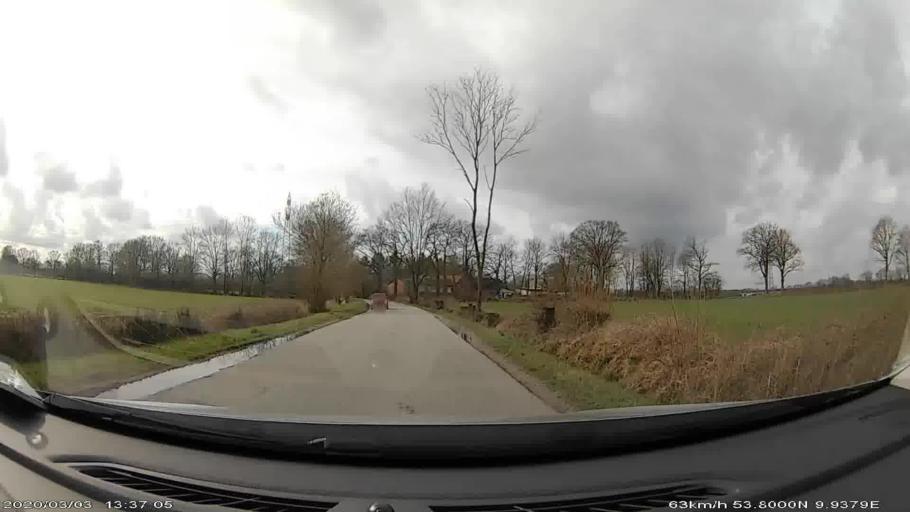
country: DE
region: Schleswig-Holstein
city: Alveslohe
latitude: 53.7998
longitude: 9.9362
